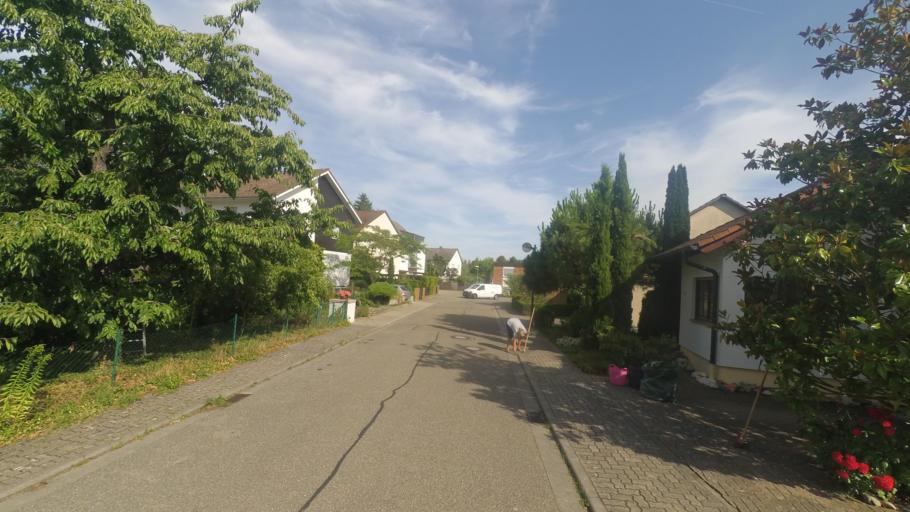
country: DE
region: Rheinland-Pfalz
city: Limburgerhof
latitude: 49.4217
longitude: 8.3820
